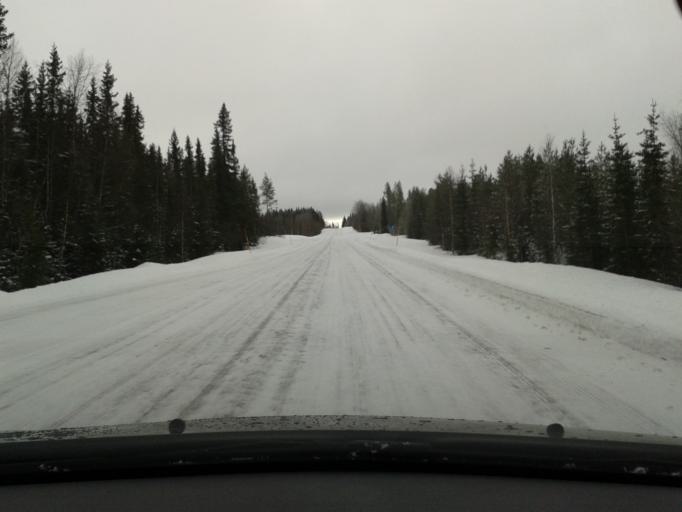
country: SE
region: Vaesterbotten
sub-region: Vilhelmina Kommun
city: Sjoberg
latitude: 64.8180
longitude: 15.9673
